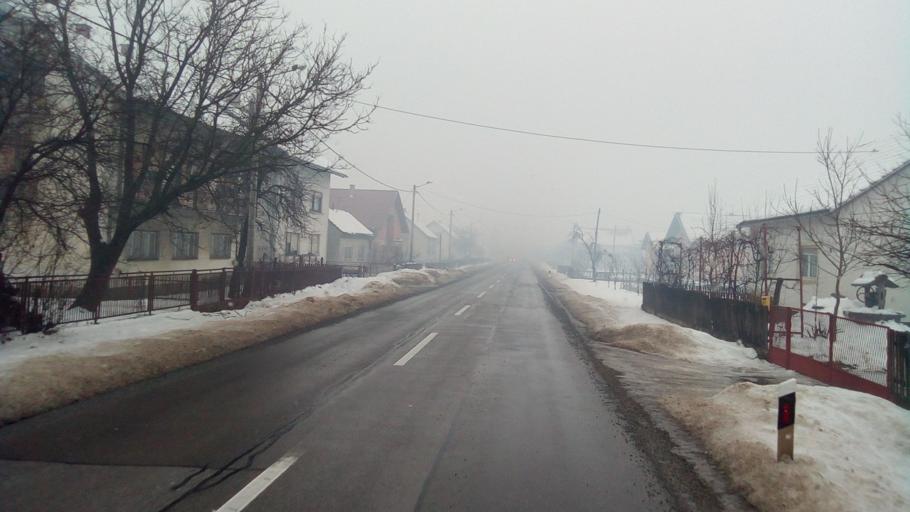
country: HR
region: Sisacko-Moslavacka
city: Petrinja
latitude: 45.4195
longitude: 16.2895
